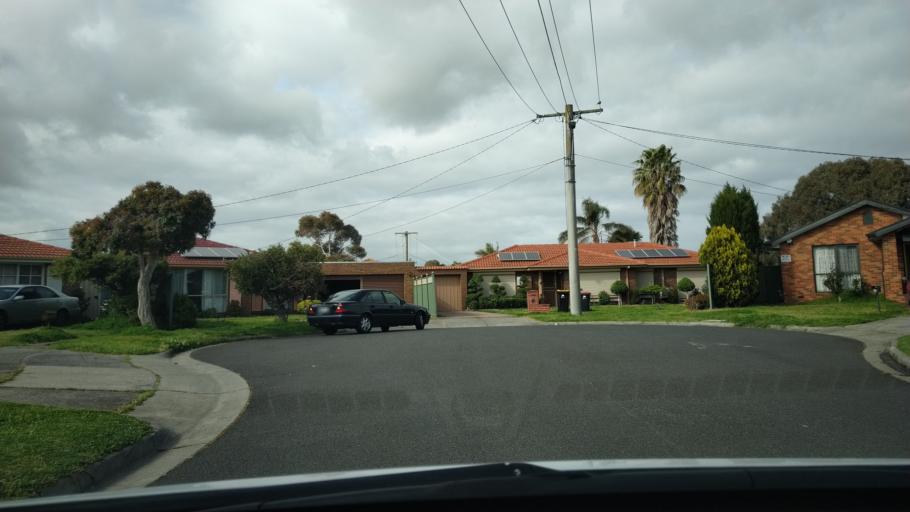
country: AU
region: Victoria
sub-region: Greater Dandenong
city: Keysborough
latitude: -37.9960
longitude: 145.1659
